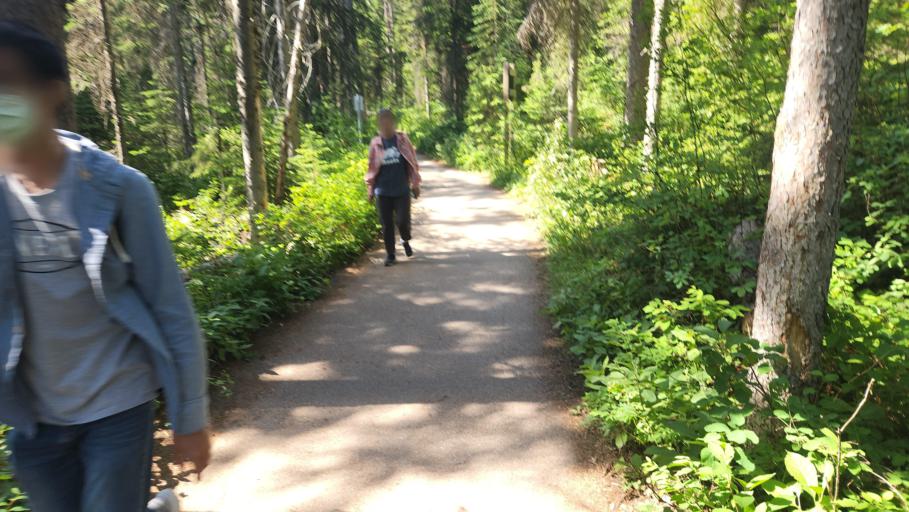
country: CA
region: Alberta
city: Lake Louise
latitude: 51.4422
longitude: -116.5425
